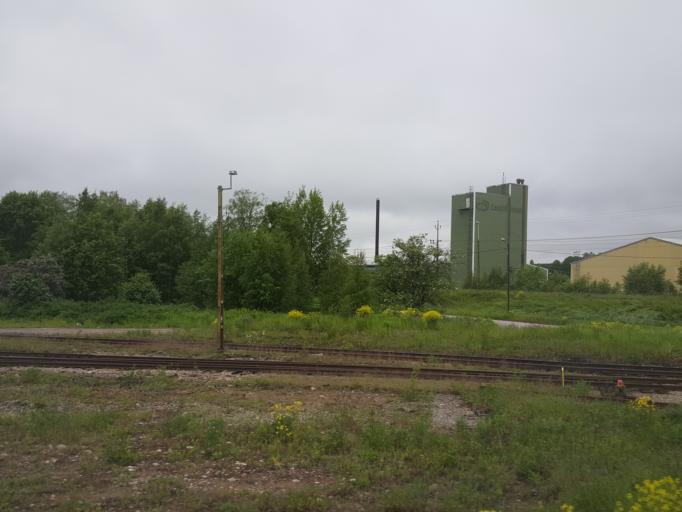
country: SE
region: Dalarna
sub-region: Avesta Kommun
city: Avesta
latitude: 60.1243
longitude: 16.2198
